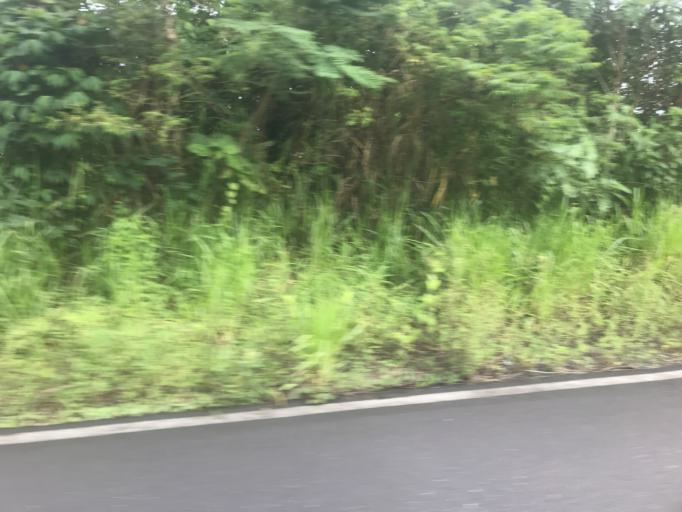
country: EC
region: Napo
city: Tena
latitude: -1.0421
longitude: -77.8046
